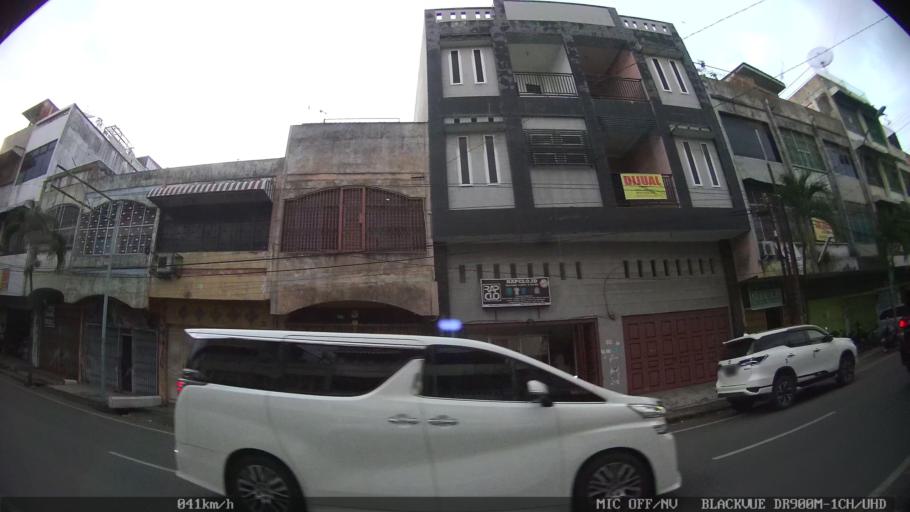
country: ID
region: North Sumatra
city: Medan
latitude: 3.5807
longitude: 98.6917
